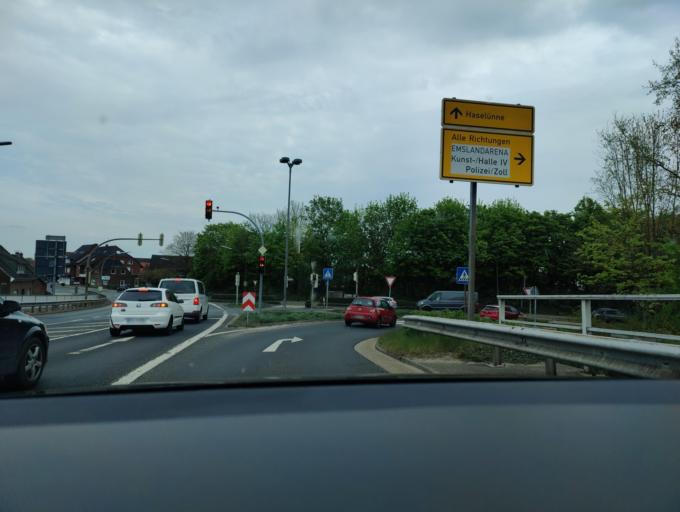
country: DE
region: Lower Saxony
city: Lingen
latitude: 52.5252
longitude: 7.3272
